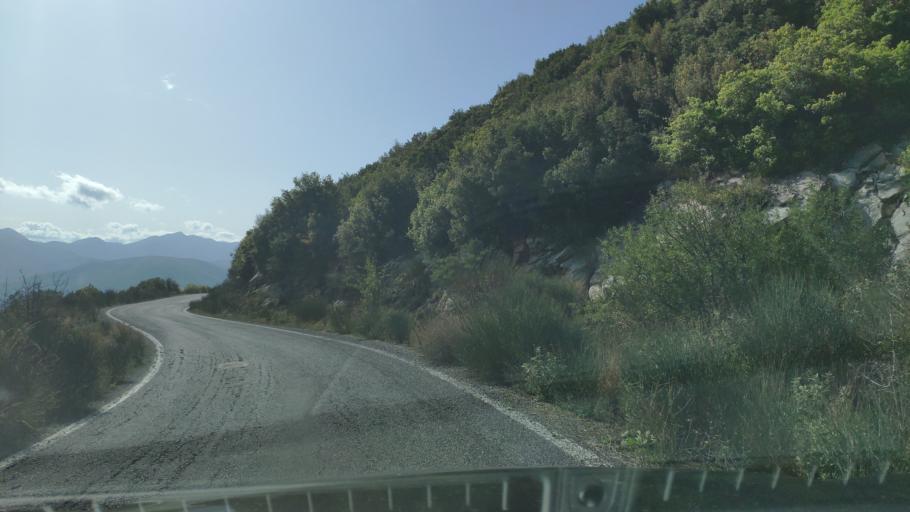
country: GR
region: Peloponnese
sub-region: Nomos Arkadias
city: Dimitsana
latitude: 37.5736
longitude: 22.0117
